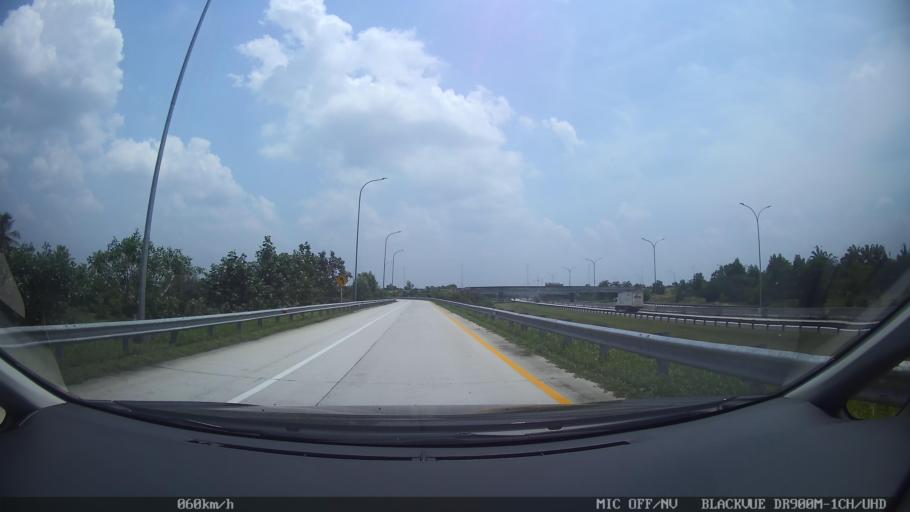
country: ID
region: Lampung
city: Natar
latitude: -5.2763
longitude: 105.2157
